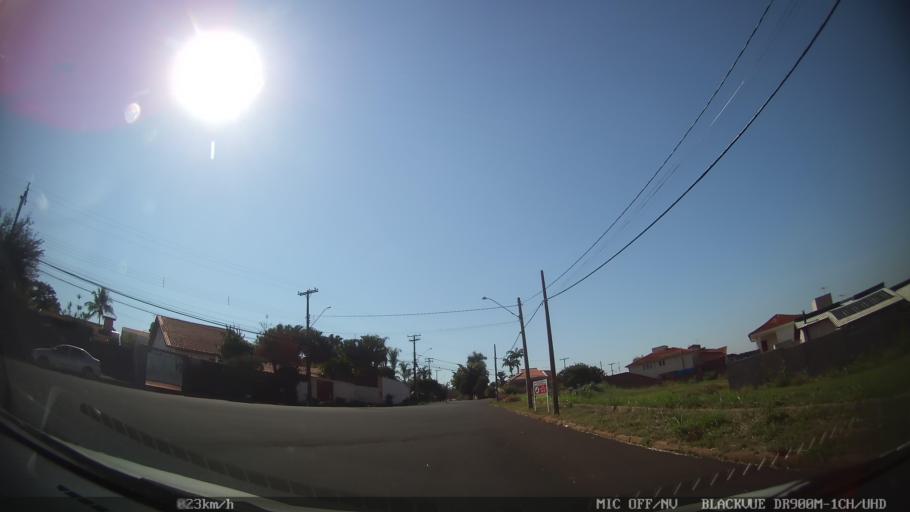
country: BR
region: Sao Paulo
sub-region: Ribeirao Preto
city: Ribeirao Preto
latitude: -21.2092
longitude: -47.7759
